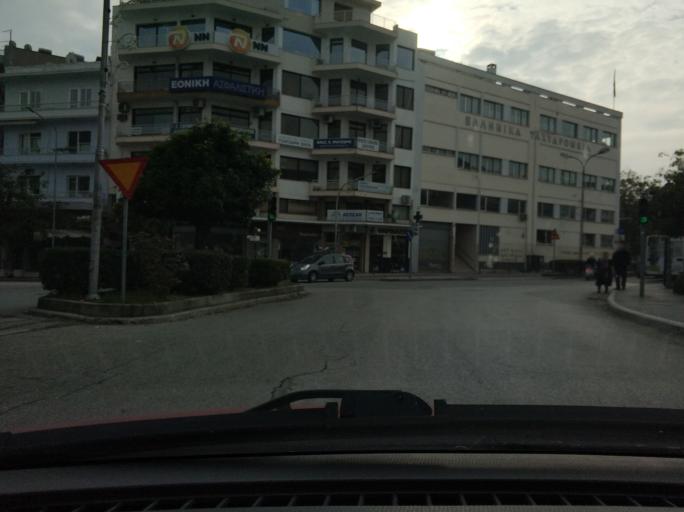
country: GR
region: East Macedonia and Thrace
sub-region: Nomos Kavalas
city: Kavala
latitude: 40.9368
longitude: 24.4090
